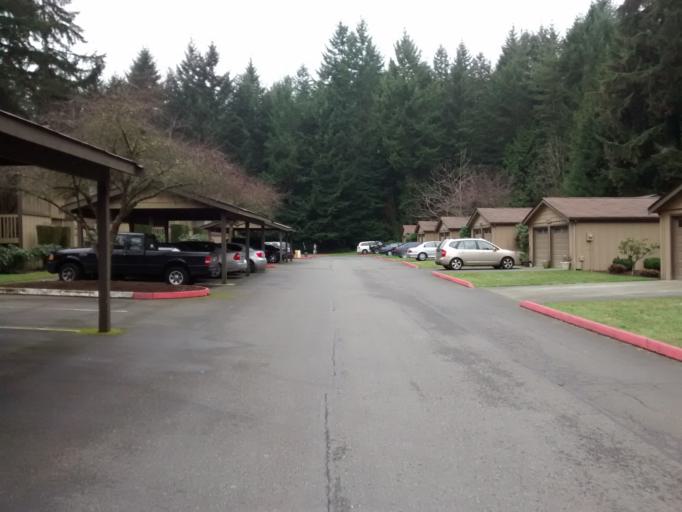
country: US
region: Washington
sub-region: Kitsap County
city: Parkwood
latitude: 47.5219
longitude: -122.6081
